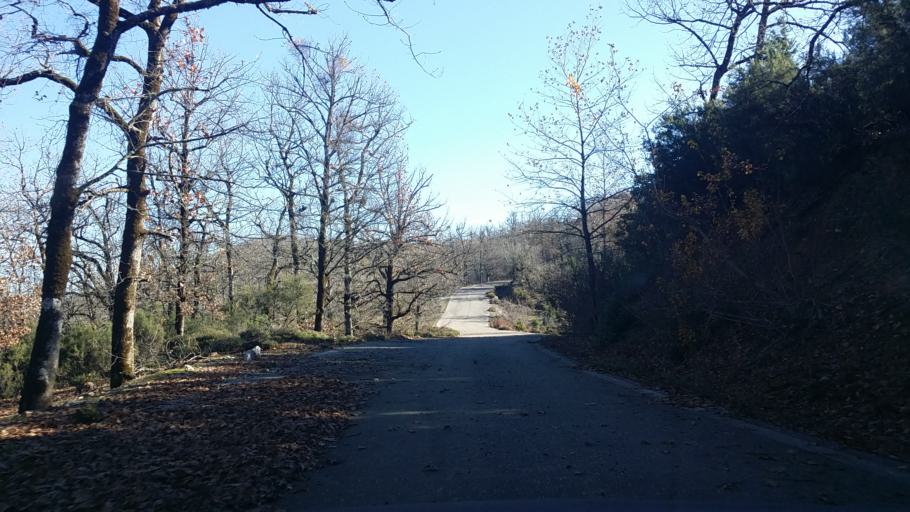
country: GR
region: West Greece
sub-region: Nomos Aitolias kai Akarnanias
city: Krikellos
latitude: 39.0185
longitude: 21.2495
